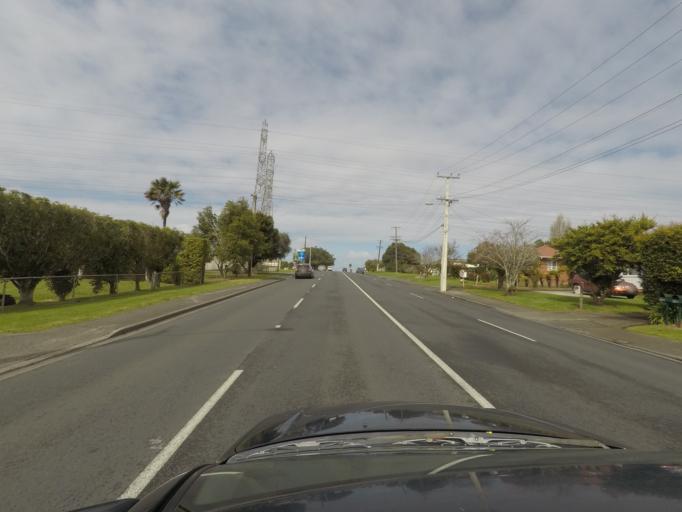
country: NZ
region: Auckland
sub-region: Auckland
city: Tamaki
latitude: -36.9064
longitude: 174.8401
